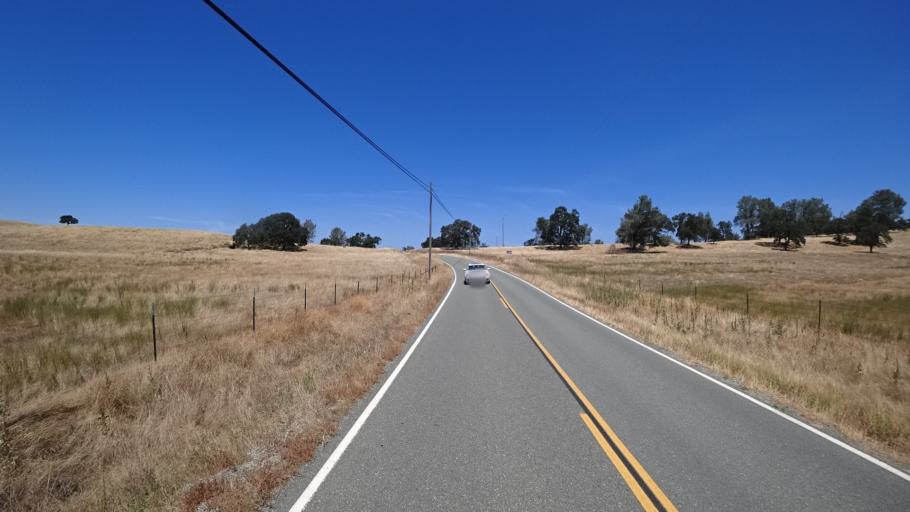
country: US
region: California
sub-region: Calaveras County
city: Valley Springs
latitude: 38.2251
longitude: -120.8347
